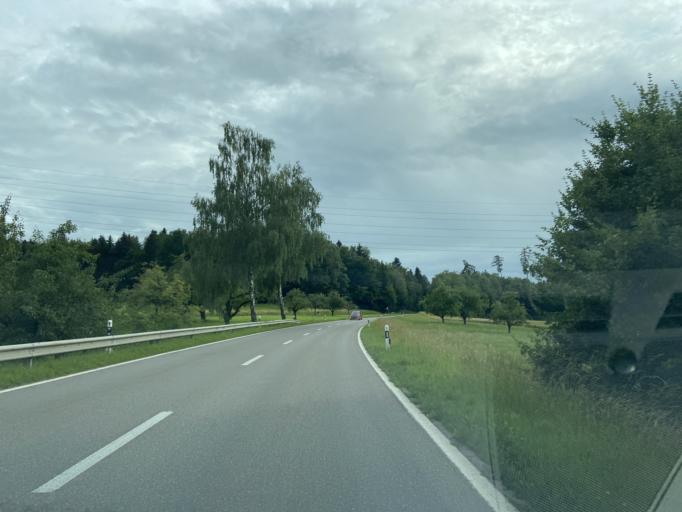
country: CH
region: Thurgau
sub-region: Muenchwilen District
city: Aadorf
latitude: 47.5028
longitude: 8.9185
